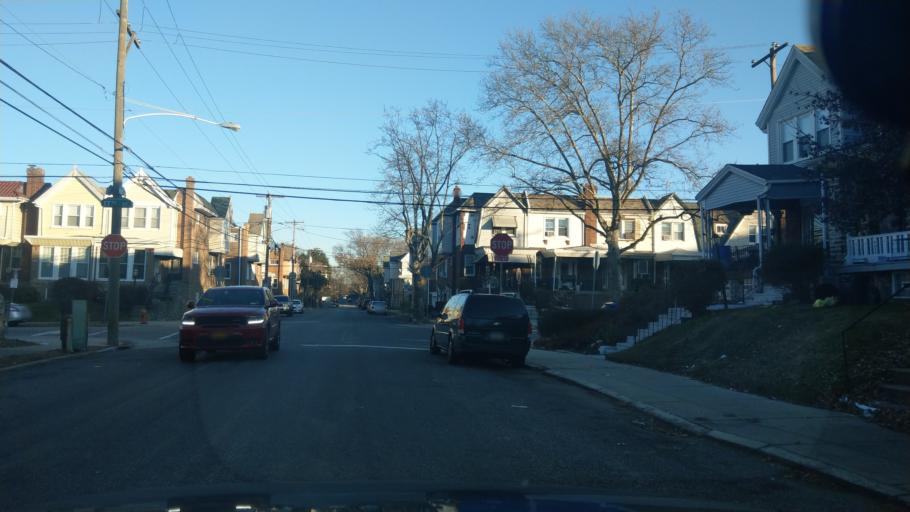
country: US
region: Pennsylvania
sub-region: Montgomery County
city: Wyncote
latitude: 40.0528
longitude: -75.1471
